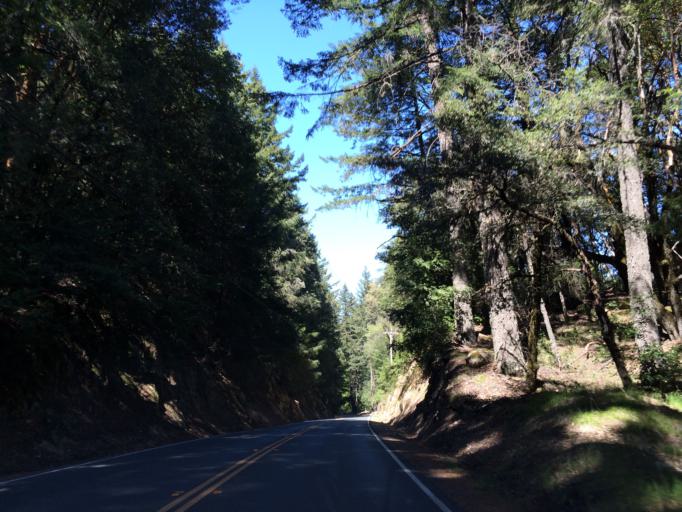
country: US
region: California
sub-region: Santa Clara County
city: Saratoga
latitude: 37.2267
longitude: -122.0931
